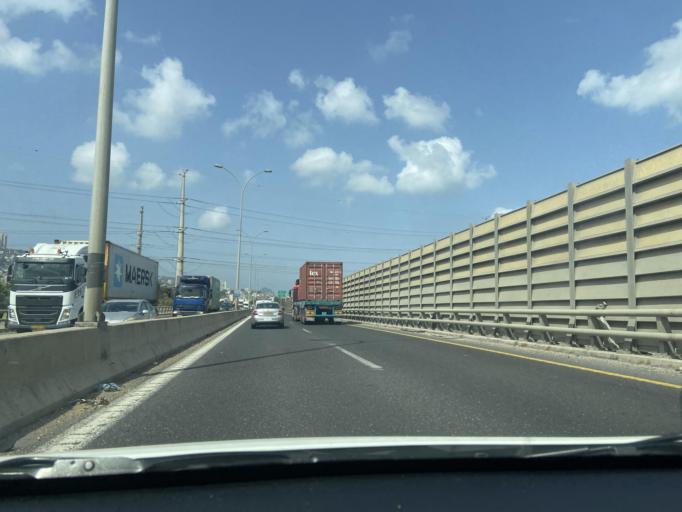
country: IL
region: Haifa
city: Haifa
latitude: 32.8010
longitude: 35.0216
